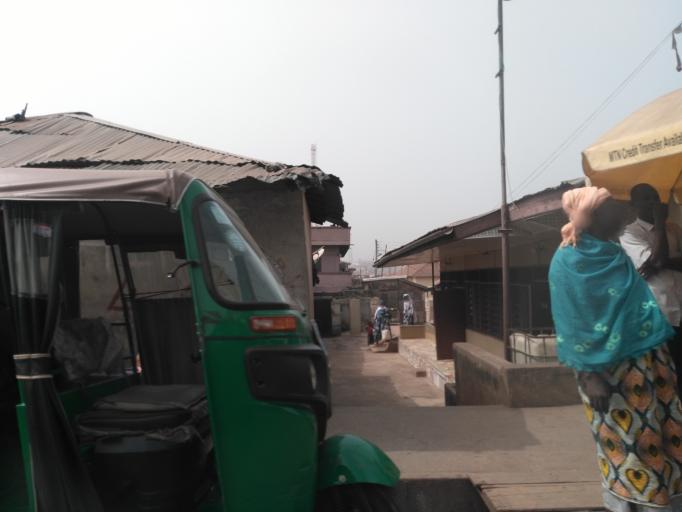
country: GH
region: Ashanti
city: Kumasi
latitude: 6.6980
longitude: -1.5963
